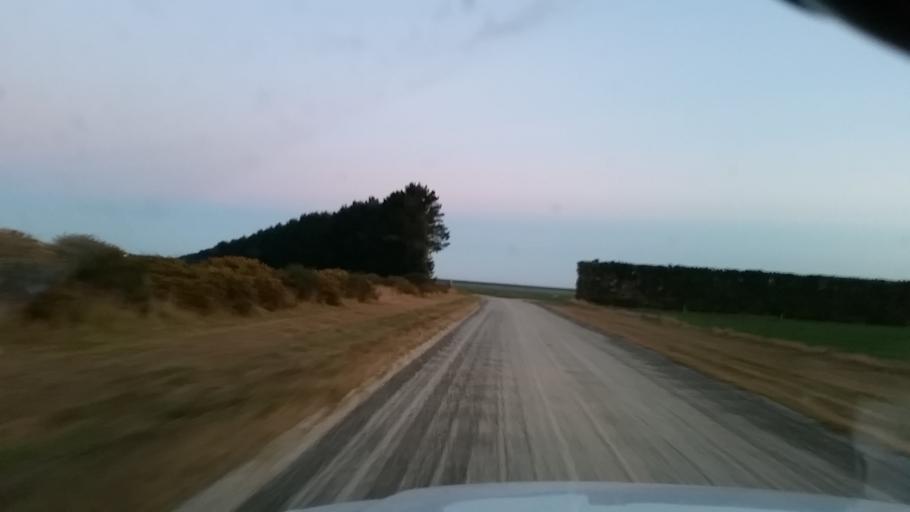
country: NZ
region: Canterbury
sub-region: Ashburton District
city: Tinwald
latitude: -43.9448
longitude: 171.6111
